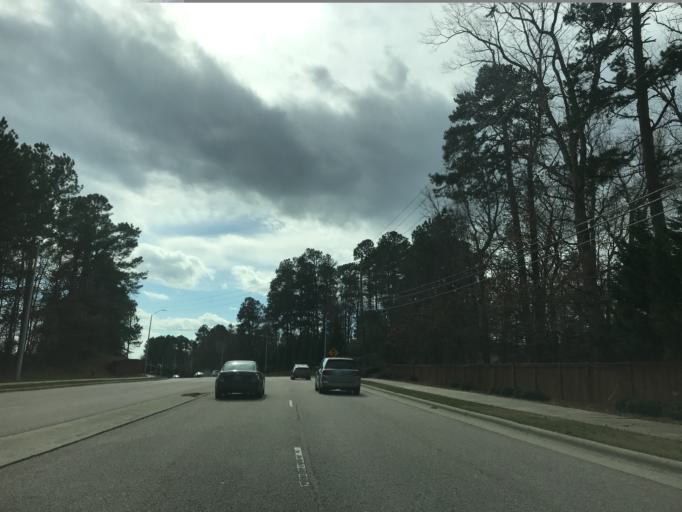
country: US
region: North Carolina
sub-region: Wake County
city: Morrisville
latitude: 35.8064
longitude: -78.8485
